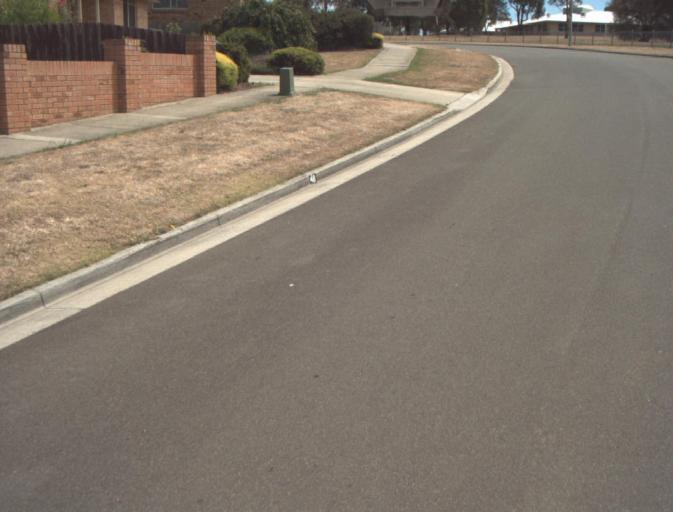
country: AU
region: Tasmania
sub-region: Launceston
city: Mayfield
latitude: -41.3805
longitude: 147.1209
